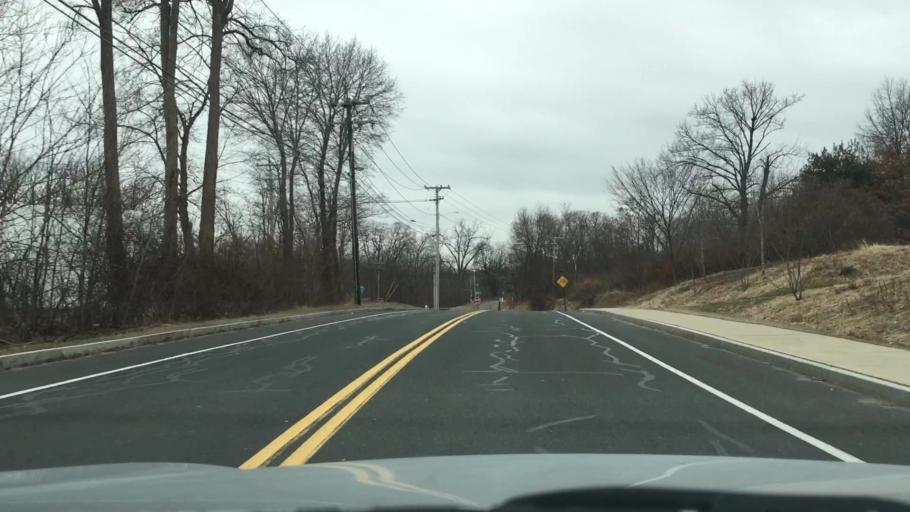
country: US
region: Massachusetts
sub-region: Hampshire County
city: Northampton
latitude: 42.3089
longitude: -72.6447
